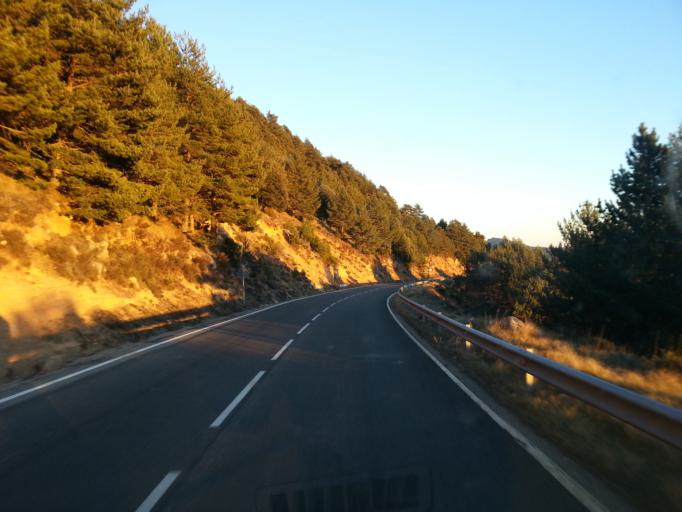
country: ES
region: Catalonia
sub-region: Provincia de Lleida
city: Olius
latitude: 42.1317
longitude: 1.5473
